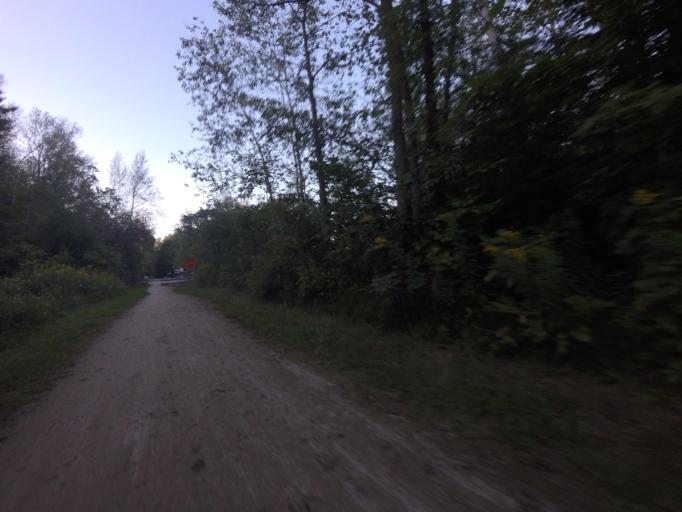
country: CA
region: Ontario
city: Brampton
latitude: 43.9196
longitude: -79.8414
